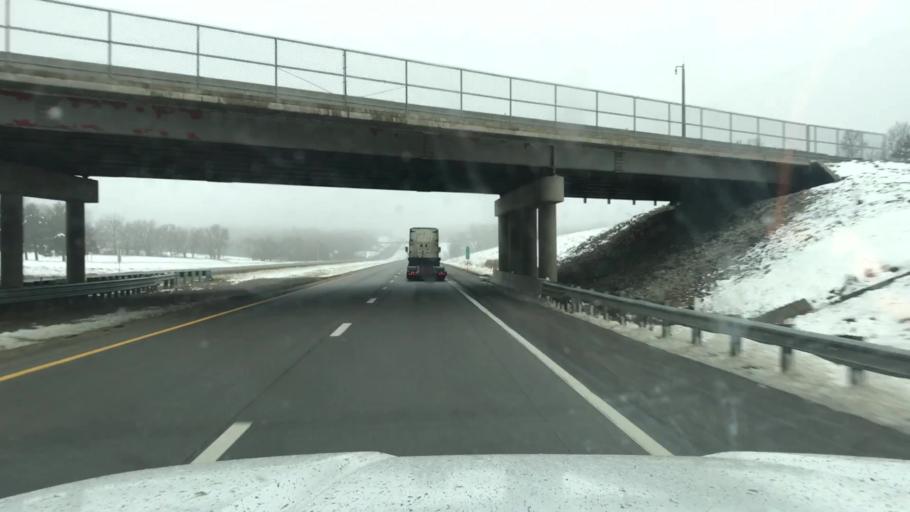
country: US
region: Missouri
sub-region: Andrew County
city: Country Club Village
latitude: 39.8150
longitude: -94.8039
